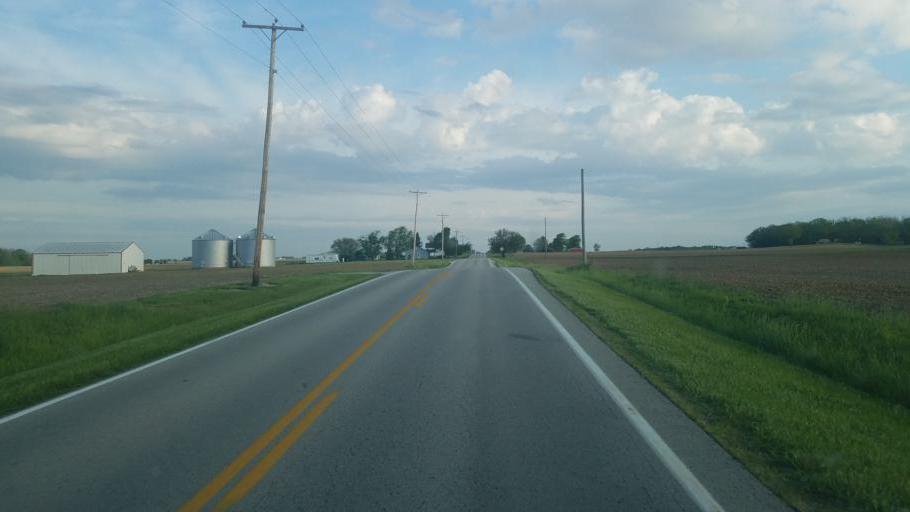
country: US
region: Ohio
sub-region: Clinton County
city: Sabina
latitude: 39.4230
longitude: -83.6216
